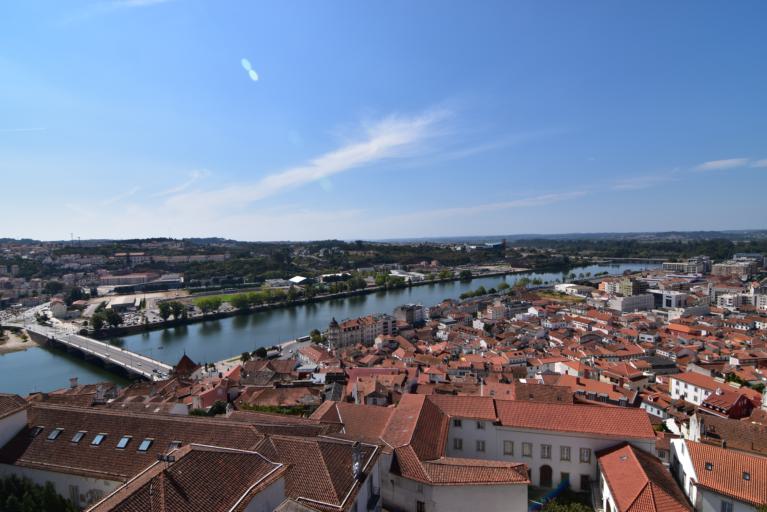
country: PT
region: Coimbra
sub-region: Coimbra
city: Coimbra
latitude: 40.2079
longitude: -8.4270
